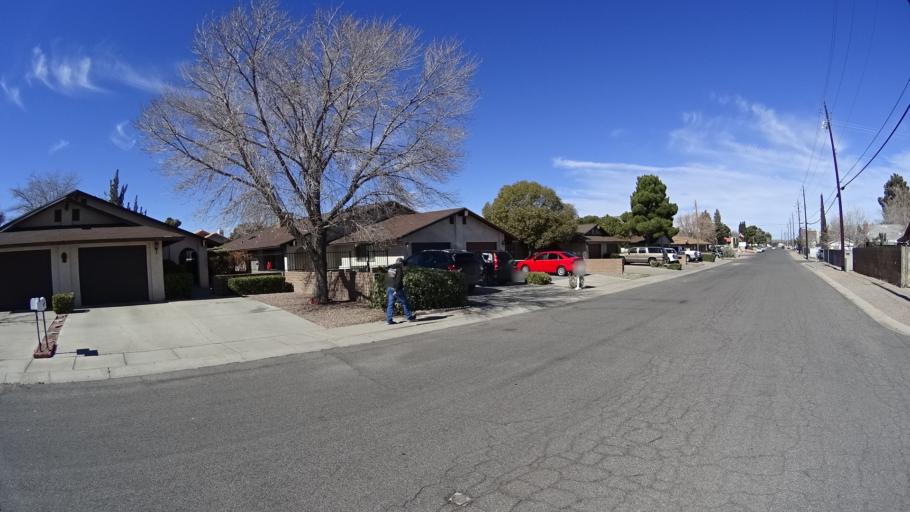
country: US
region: Arizona
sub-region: Mohave County
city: Kingman
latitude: 35.2117
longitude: -114.0401
